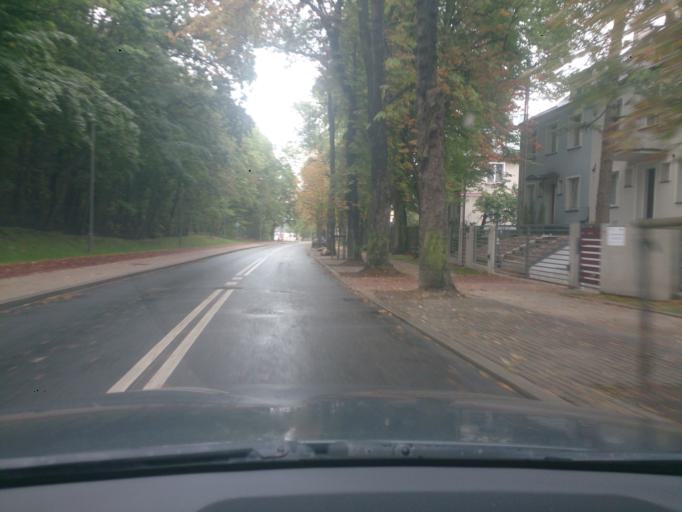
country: PL
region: Pomeranian Voivodeship
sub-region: Sopot
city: Sopot
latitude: 54.4466
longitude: 18.5523
